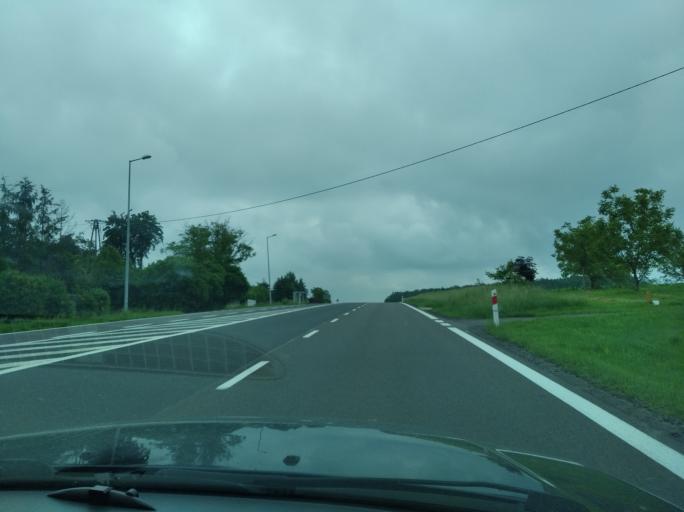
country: PL
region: Subcarpathian Voivodeship
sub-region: Powiat przeworski
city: Nowosielce
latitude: 50.0652
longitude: 22.4139
